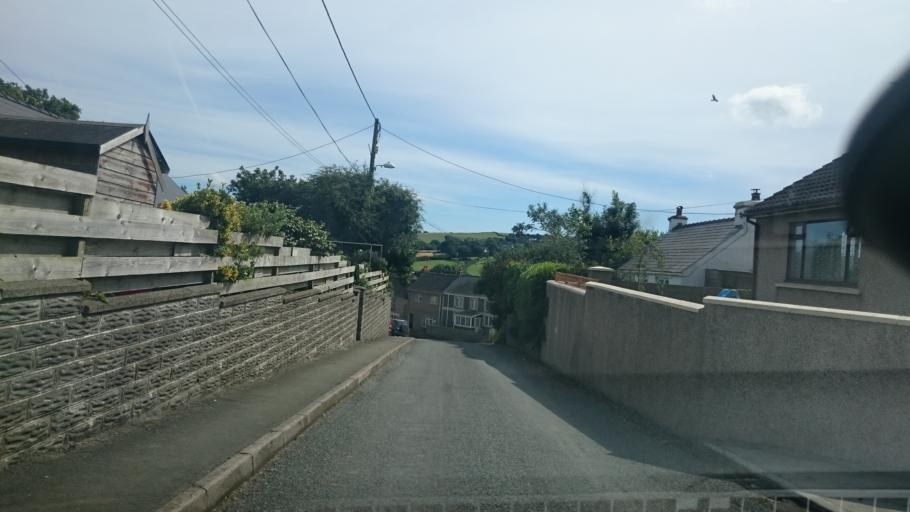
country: GB
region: Wales
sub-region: Pembrokeshire
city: Llangwm
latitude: 51.7499
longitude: -4.9149
